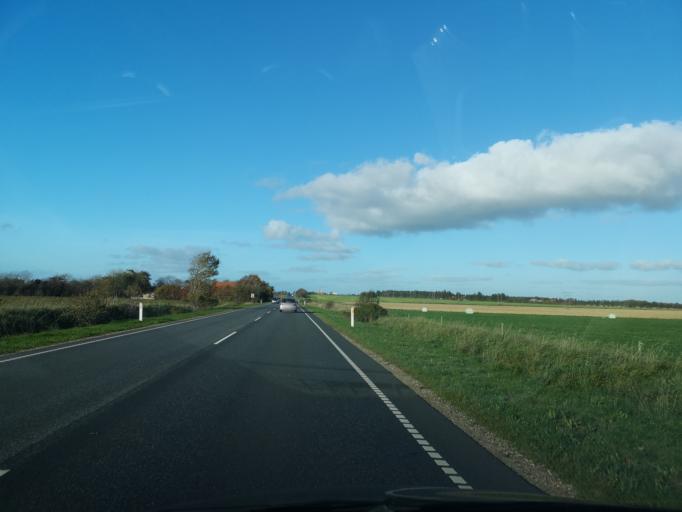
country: DK
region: South Denmark
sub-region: Varde Kommune
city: Varde
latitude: 55.7432
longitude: 8.4937
